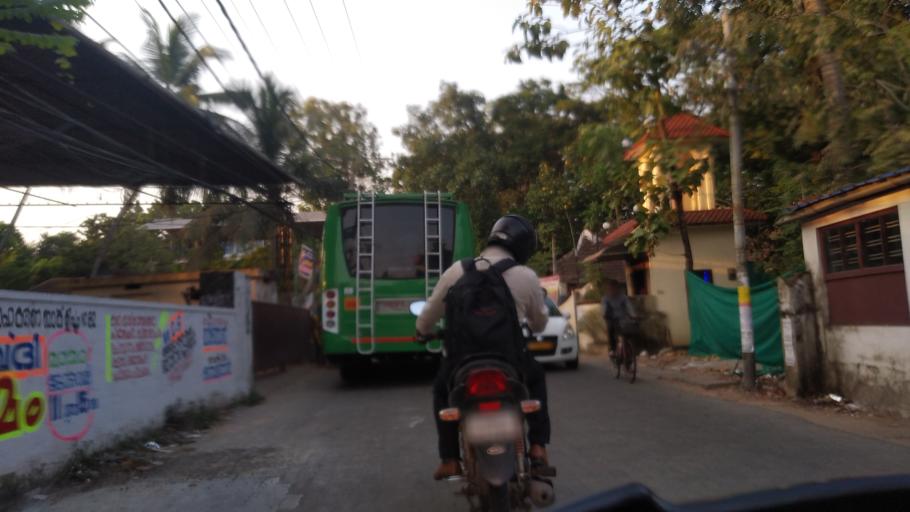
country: IN
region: Kerala
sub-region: Ernakulam
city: Elur
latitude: 10.0304
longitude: 76.2752
